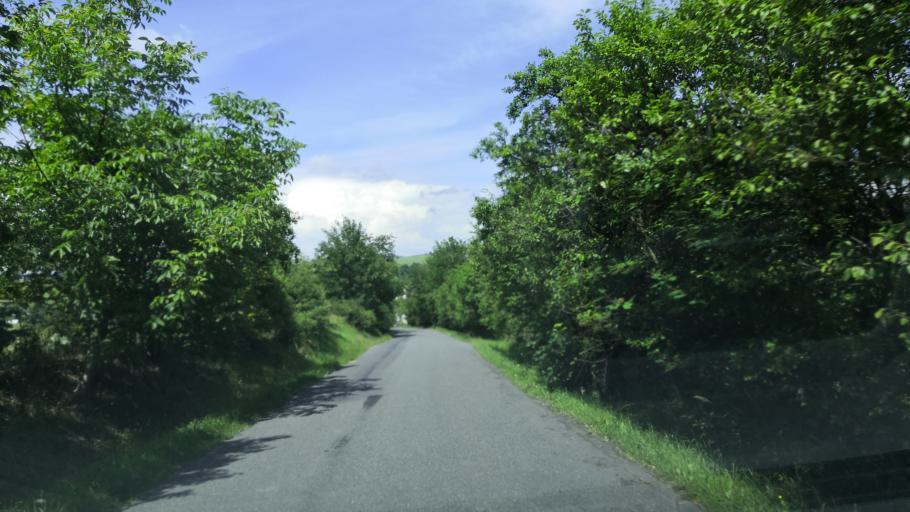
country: CZ
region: Zlin
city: Vidce
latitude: 49.4379
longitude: 18.0941
